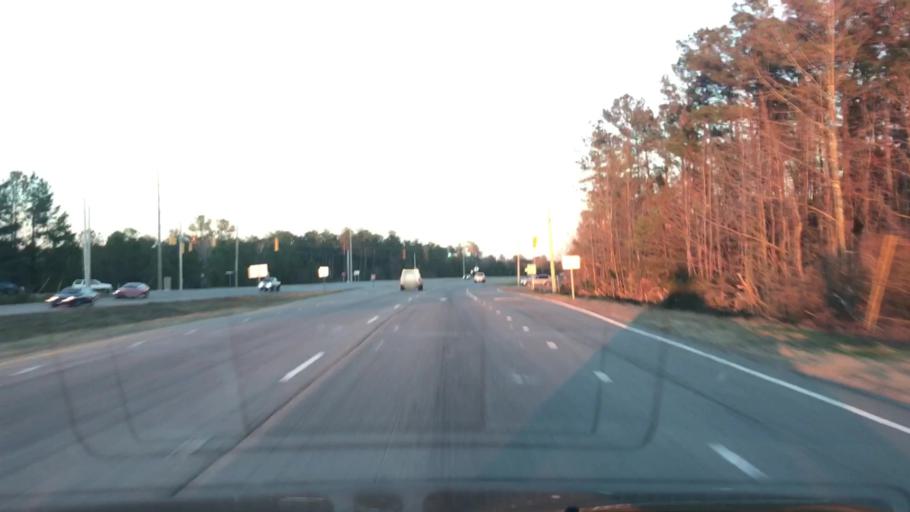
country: US
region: North Carolina
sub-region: Brunswick County
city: Shallotte
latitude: 33.9869
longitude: -78.3911
